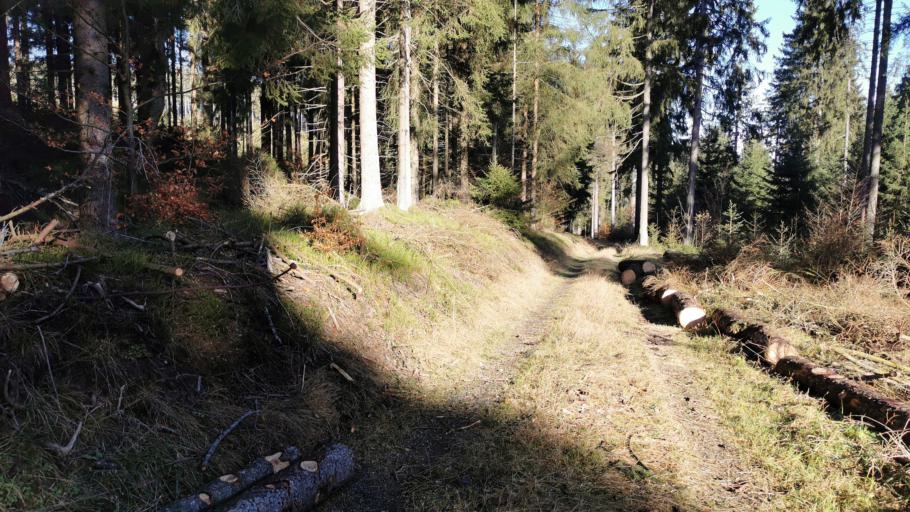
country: DE
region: Bavaria
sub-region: Upper Franconia
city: Reichenbach
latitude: 50.4467
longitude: 11.4286
